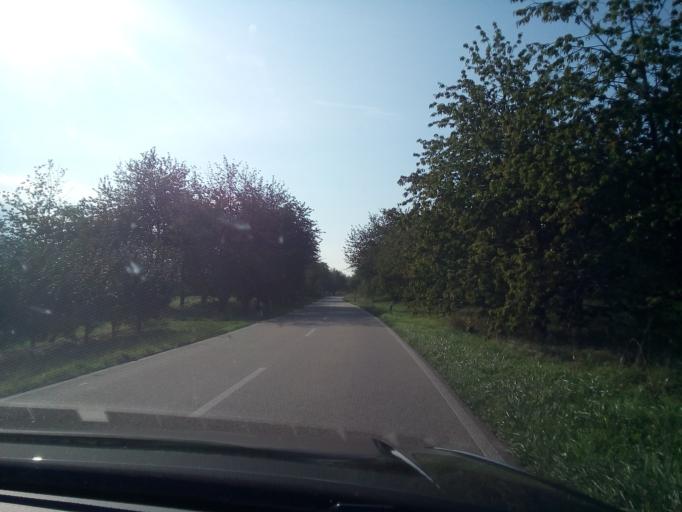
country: DE
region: Baden-Wuerttemberg
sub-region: Freiburg Region
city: Haslach
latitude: 48.5608
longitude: 8.0468
